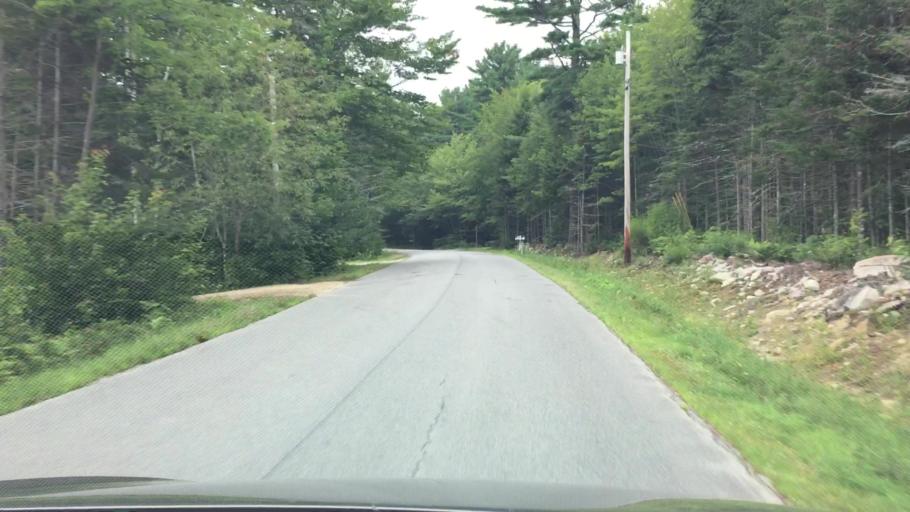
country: US
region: Maine
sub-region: Waldo County
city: Stockton Springs
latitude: 44.5170
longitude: -68.8762
